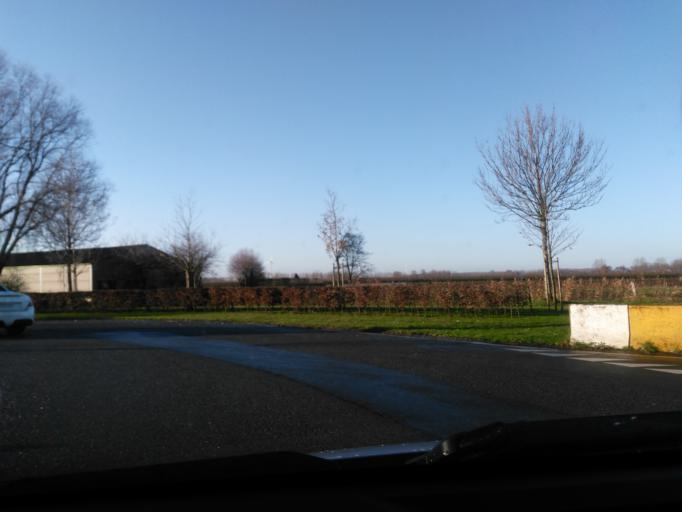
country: BE
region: Flanders
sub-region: Provincie Oost-Vlaanderen
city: Sint-Gillis-Waas
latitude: 51.2470
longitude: 4.1903
